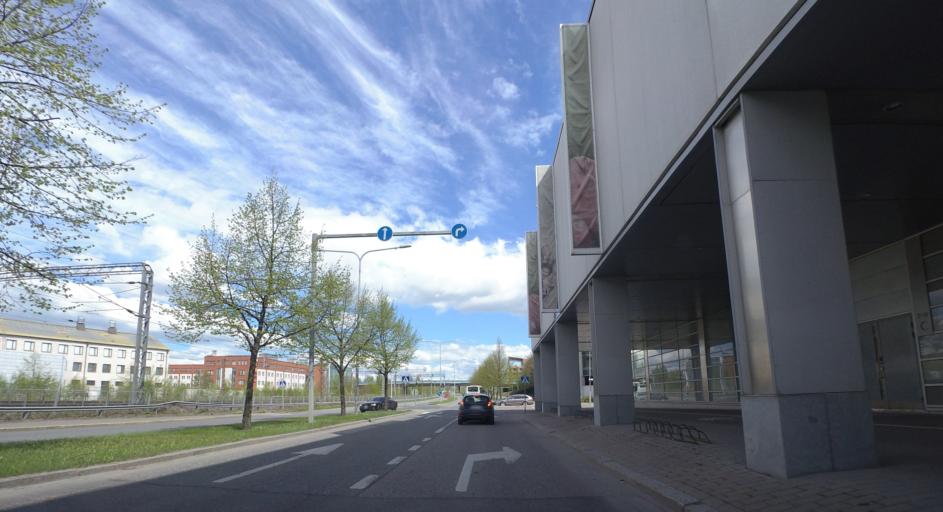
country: FI
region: Uusimaa
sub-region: Helsinki
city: Vantaa
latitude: 60.2524
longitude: 25.0140
